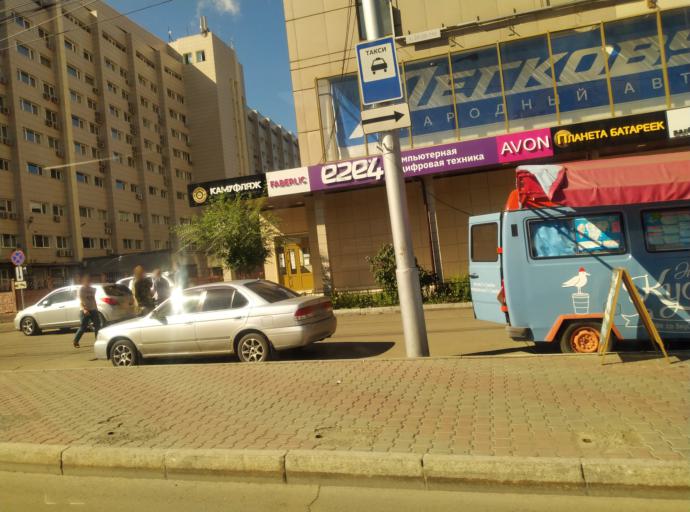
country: RU
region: Krasnoyarskiy
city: Krasnoyarsk
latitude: 56.0099
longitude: 92.8712
